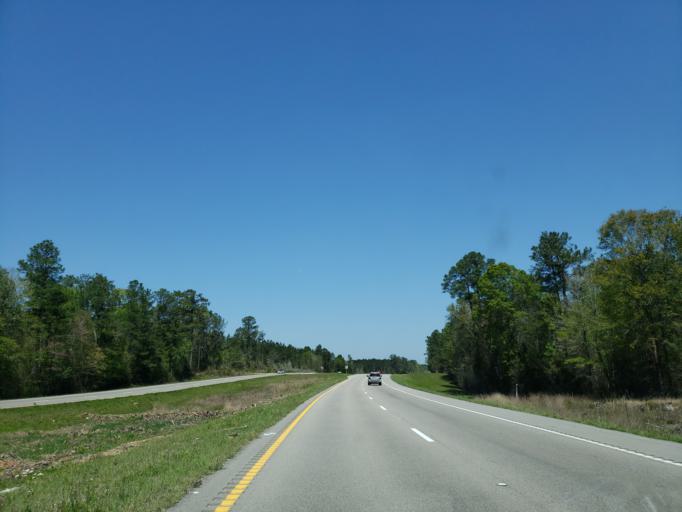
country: US
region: Mississippi
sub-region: Stone County
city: Wiggins
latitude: 30.9817
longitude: -89.2004
